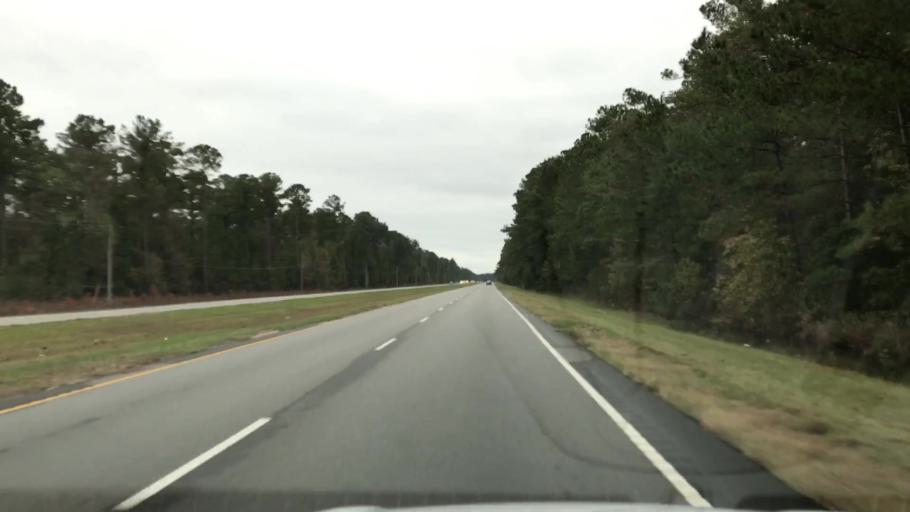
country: US
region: South Carolina
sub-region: Georgetown County
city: Georgetown
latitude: 33.2565
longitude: -79.3702
